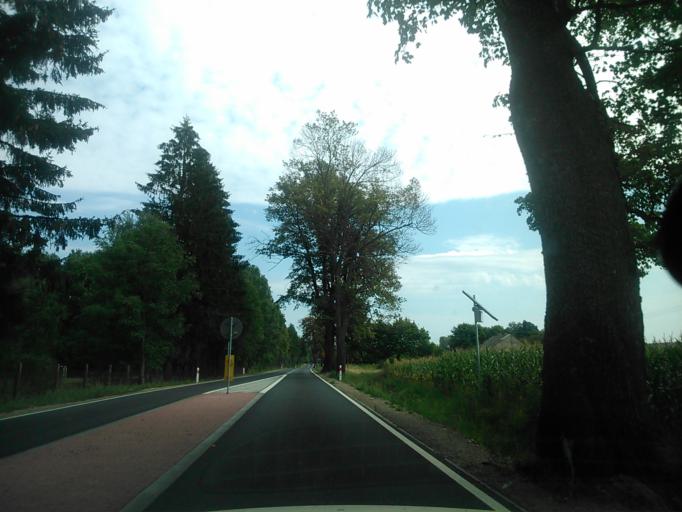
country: PL
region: Warmian-Masurian Voivodeship
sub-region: Powiat dzialdowski
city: Dzialdowo
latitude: 53.2342
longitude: 20.0420
